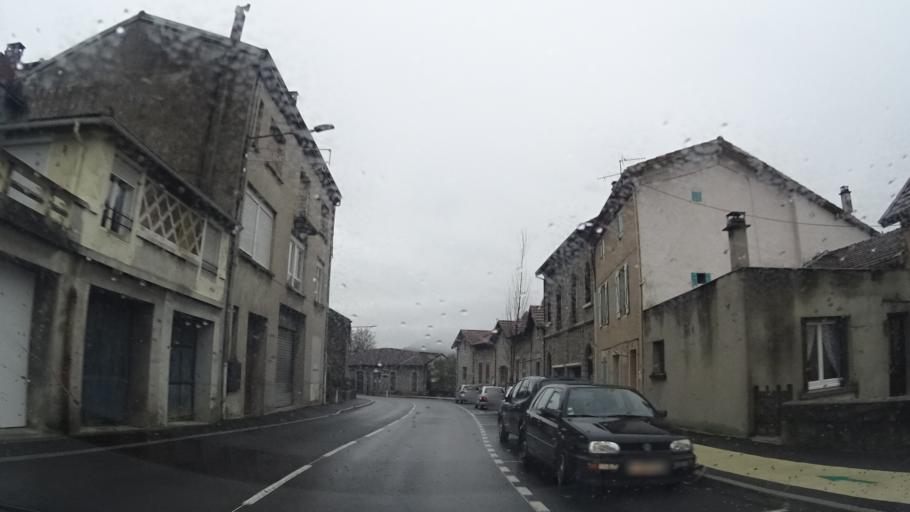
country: FR
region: Rhone-Alpes
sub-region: Departement de l'Ardeche
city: Vals-les-Bains
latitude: 44.6631
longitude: 4.3682
